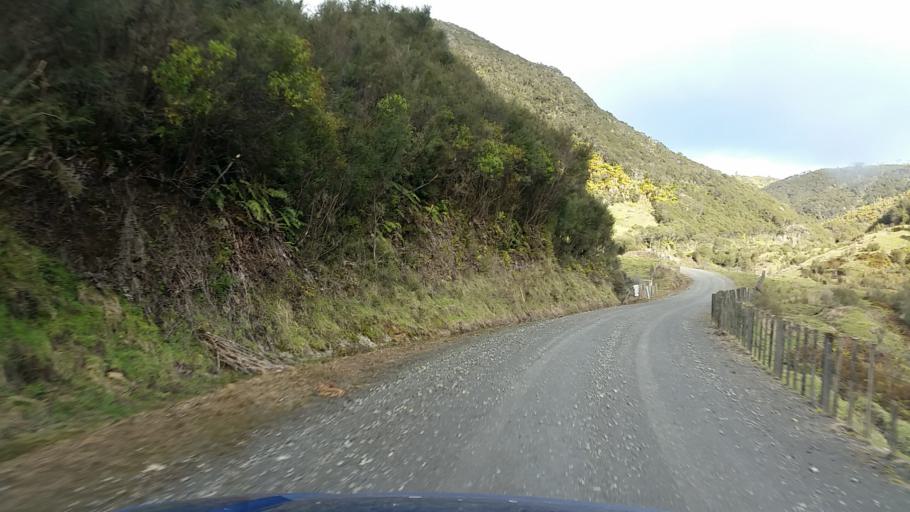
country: NZ
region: Taranaki
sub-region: South Taranaki District
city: Eltham
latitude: -39.2657
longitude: 174.7442
